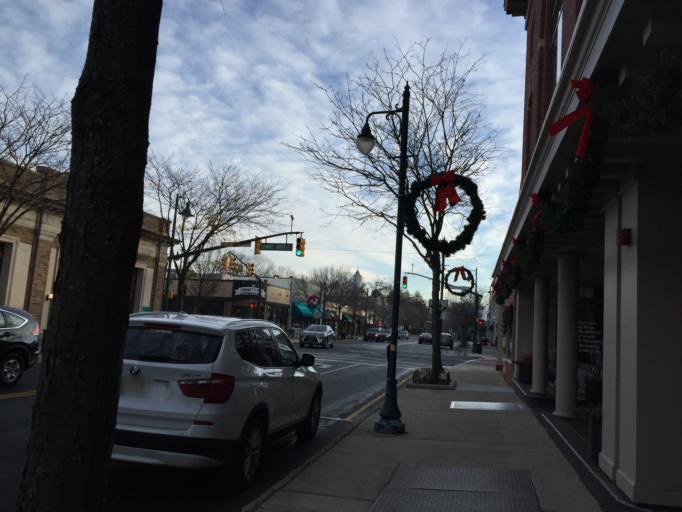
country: US
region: New Jersey
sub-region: Union County
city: Summit
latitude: 40.7180
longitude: -74.3567
